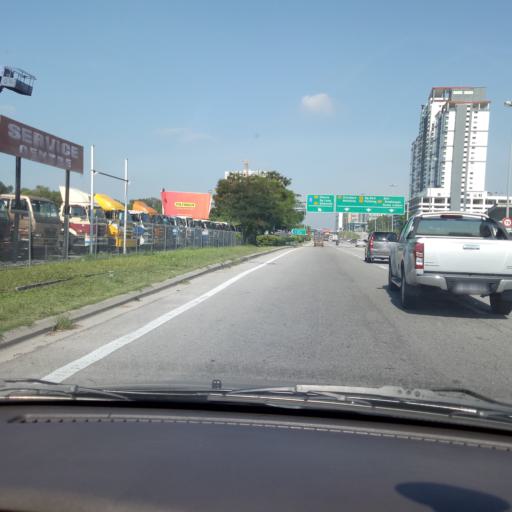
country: MY
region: Selangor
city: Kampong Baharu Balakong
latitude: 3.0299
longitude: 101.7620
